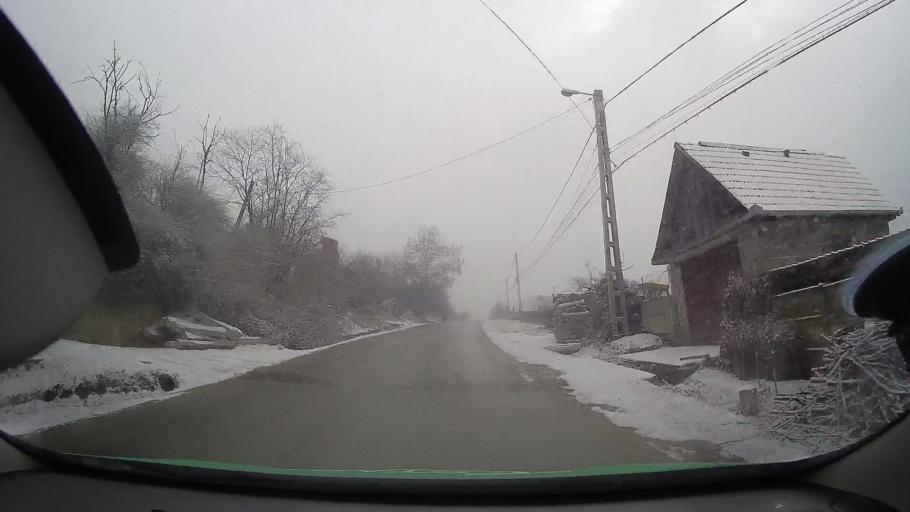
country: RO
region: Alba
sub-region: Comuna Lopadea Noua
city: Lopadea Noua
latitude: 46.2940
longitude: 23.8166
